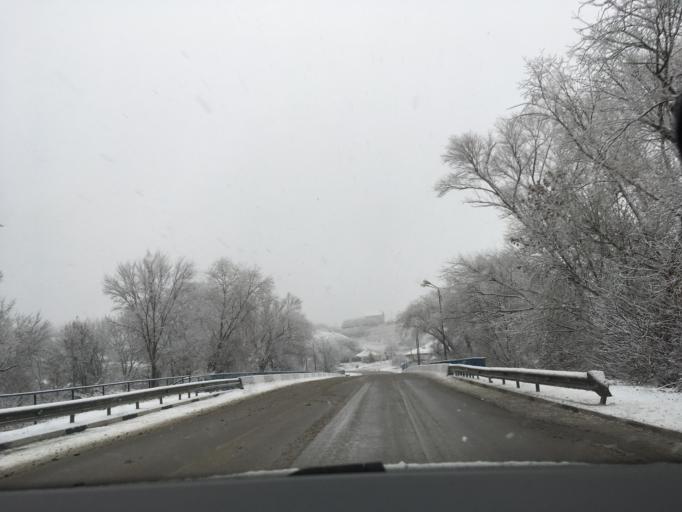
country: RU
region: Belgorod
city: Valuyki
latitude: 50.2093
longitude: 38.1092
